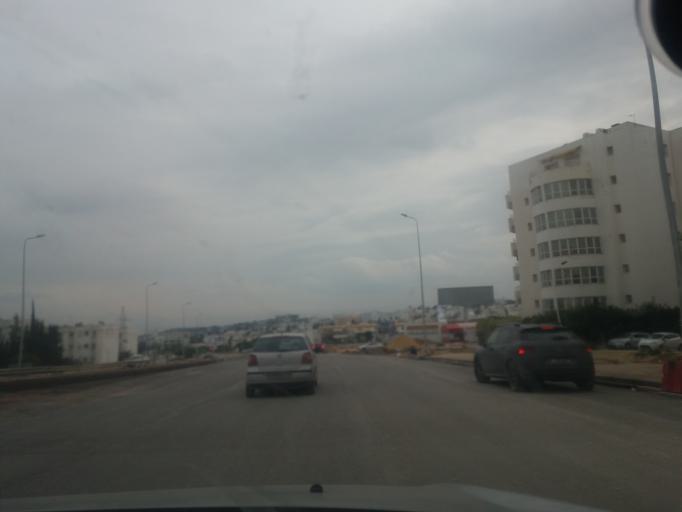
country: TN
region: Tunis
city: Tunis
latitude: 36.8537
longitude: 10.1526
